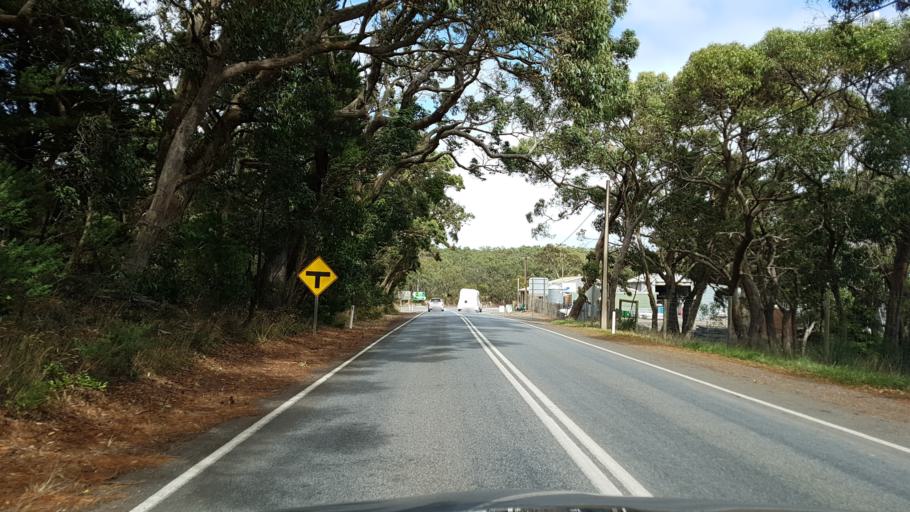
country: AU
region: South Australia
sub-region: Alexandrina
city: Mount Compass
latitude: -35.2912
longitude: 138.5819
